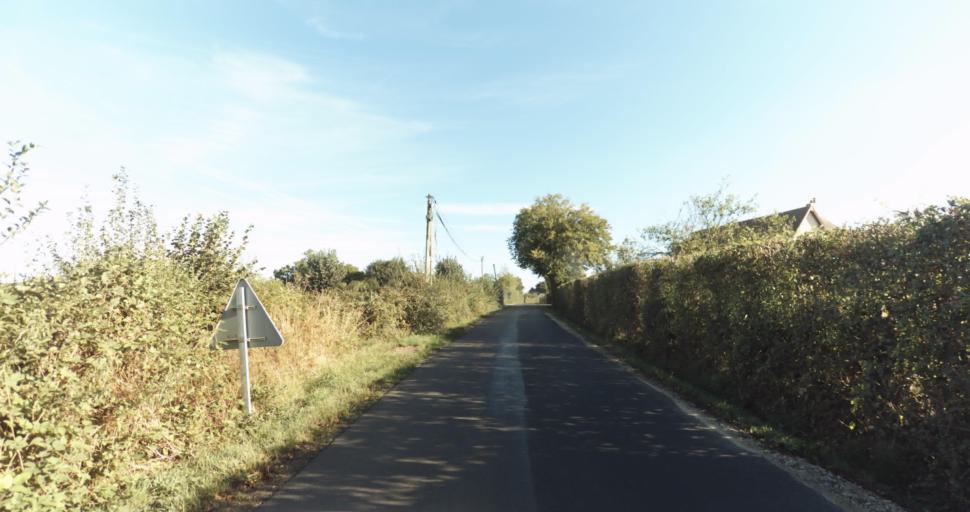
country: FR
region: Lower Normandy
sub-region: Departement de l'Orne
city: Vimoutiers
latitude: 48.9008
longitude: 0.1361
